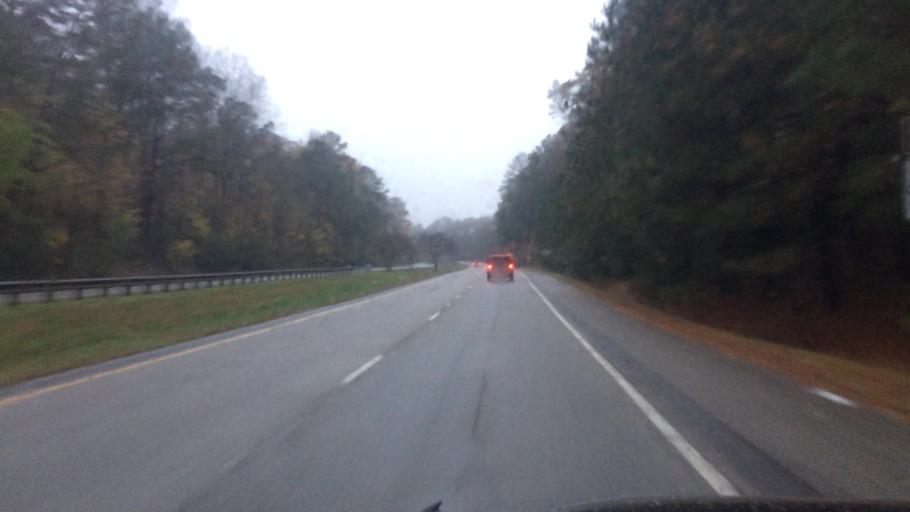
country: US
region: Virginia
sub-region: City of Williamsburg
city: Williamsburg
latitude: 37.2483
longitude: -76.6940
